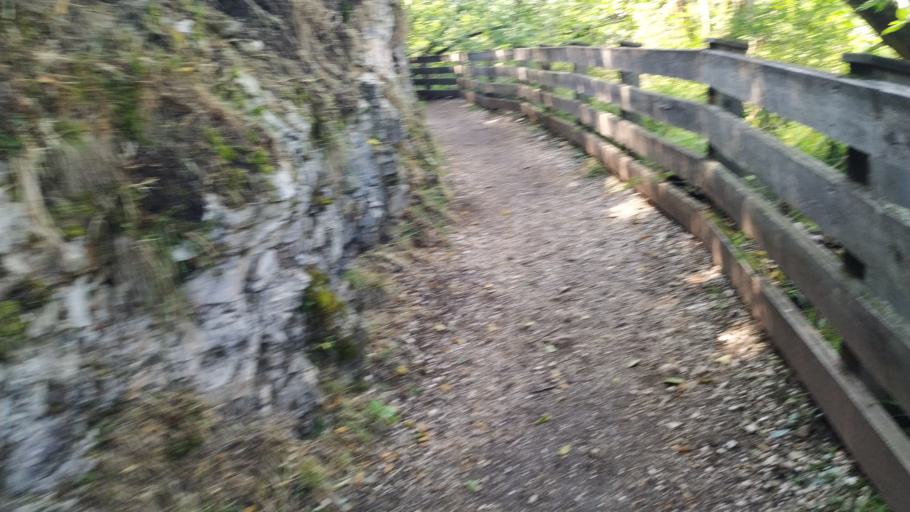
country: IT
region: Trentino-Alto Adige
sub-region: Provincia di Trento
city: Sanzeno
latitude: 46.3697
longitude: 11.0846
